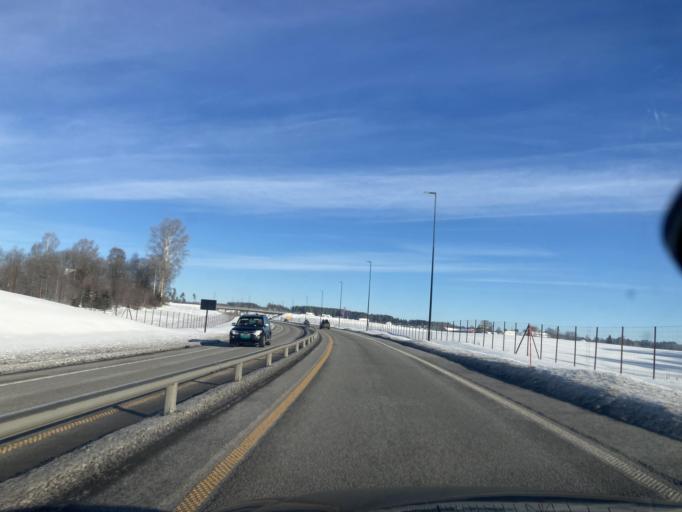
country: NO
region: Hedmark
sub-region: Loten
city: Loten
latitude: 60.8223
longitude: 11.2916
